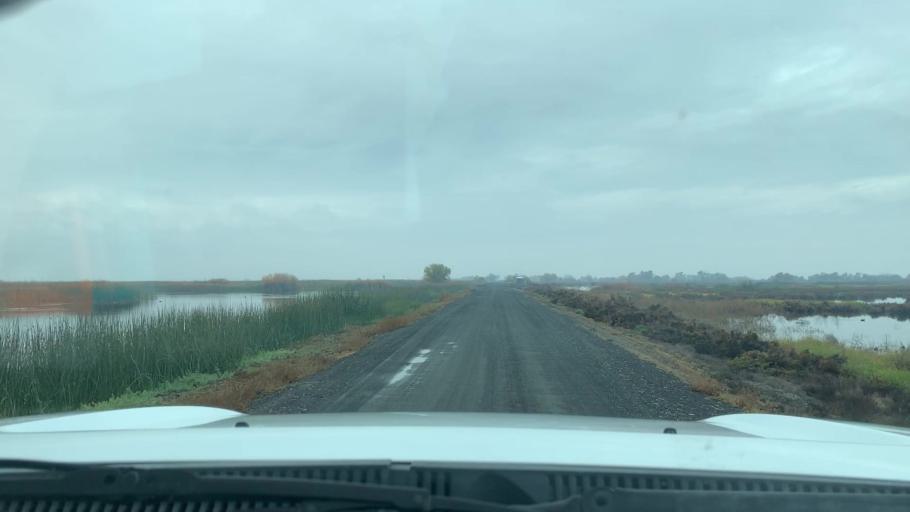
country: US
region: California
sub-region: Kern County
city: Lost Hills
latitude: 35.7336
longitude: -119.5866
